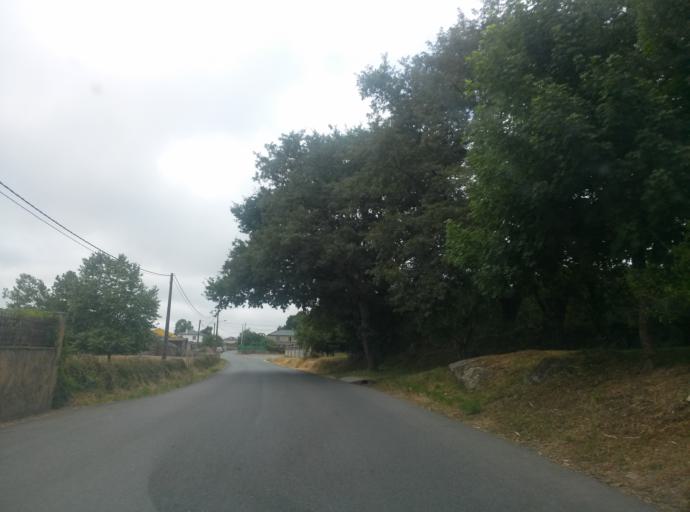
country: ES
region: Galicia
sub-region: Provincia de Lugo
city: Lugo
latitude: 43.0548
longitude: -7.5650
